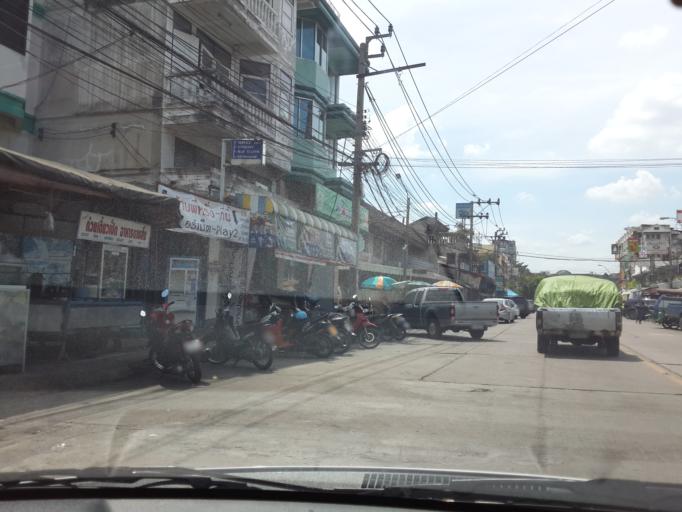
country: TH
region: Bangkok
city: Lak Si
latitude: 13.8736
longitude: 100.5807
